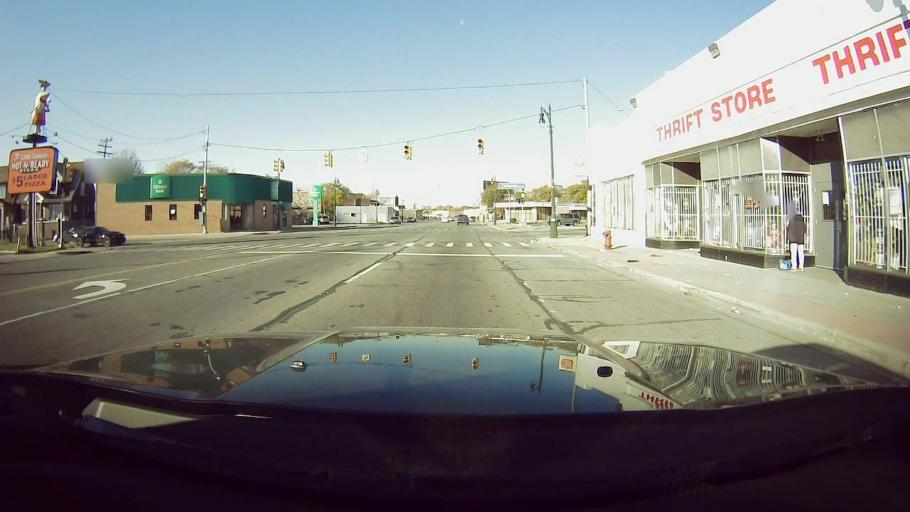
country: US
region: Michigan
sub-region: Wayne County
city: Dearborn
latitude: 42.3312
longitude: -83.1383
